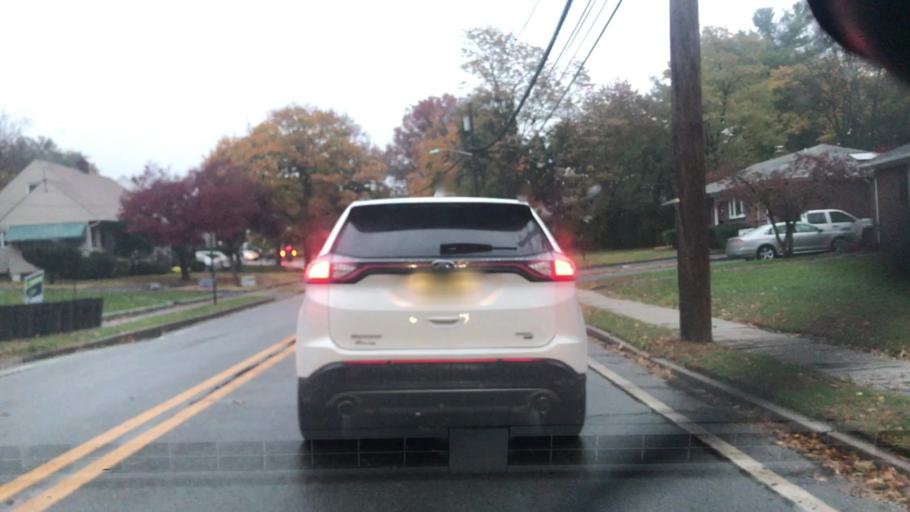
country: US
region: New Jersey
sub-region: Bergen County
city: Fair Lawn
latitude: 40.9243
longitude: -74.1298
